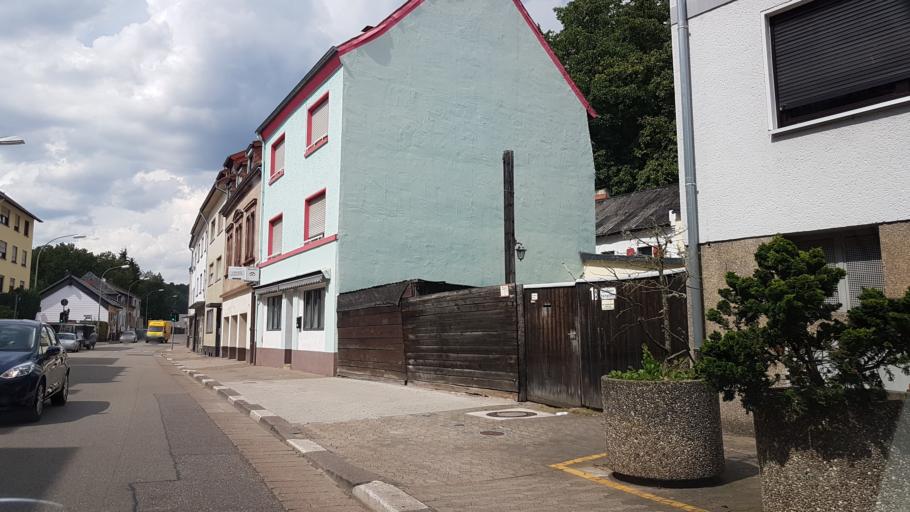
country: DE
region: Saarland
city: Saarbrucken
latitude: 49.2539
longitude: 6.9757
